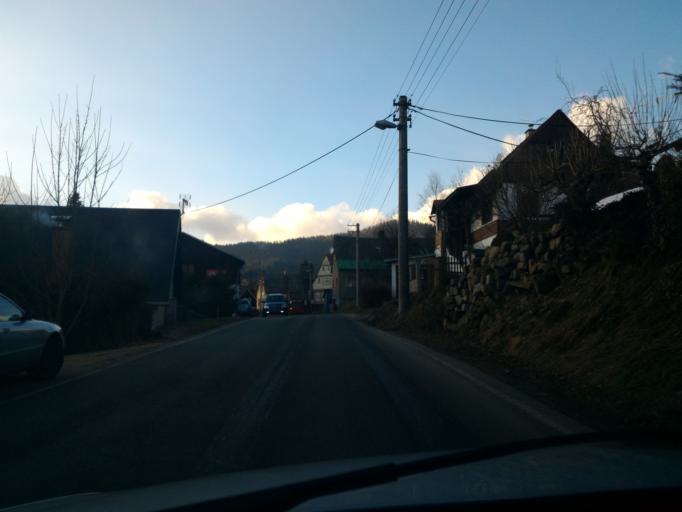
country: CZ
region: Liberecky
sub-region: Okres Jablonec nad Nisou
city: Smrzovka
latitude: 50.7392
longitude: 15.2734
